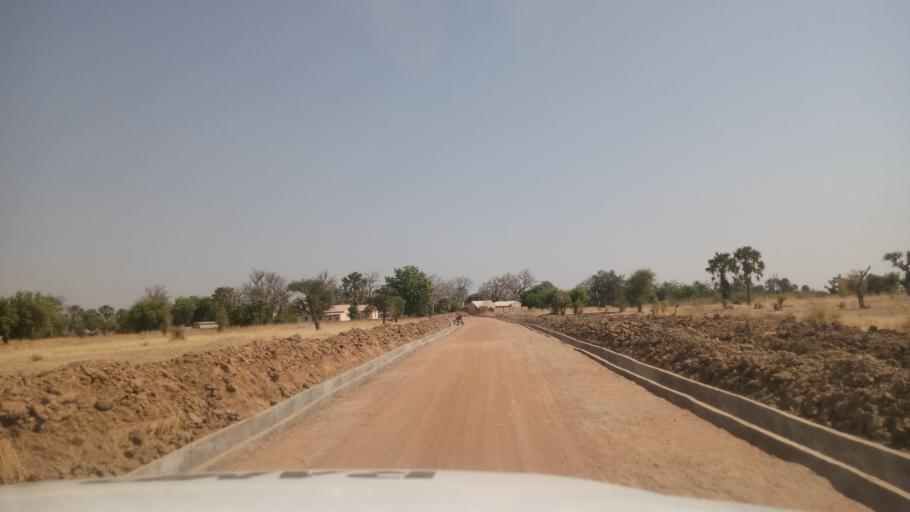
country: NG
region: Adamawa
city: Ngurore
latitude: 9.1710
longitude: 12.1996
